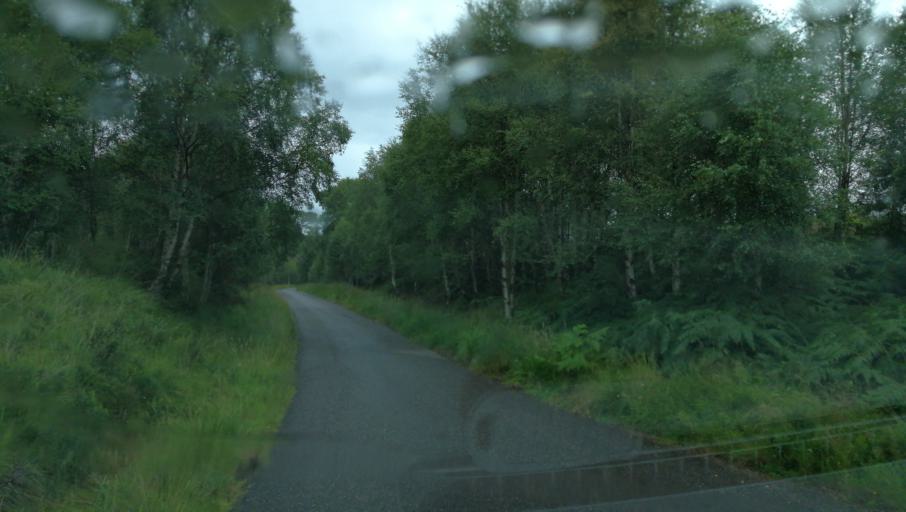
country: GB
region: Scotland
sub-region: Highland
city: Spean Bridge
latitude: 57.2669
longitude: -4.9755
